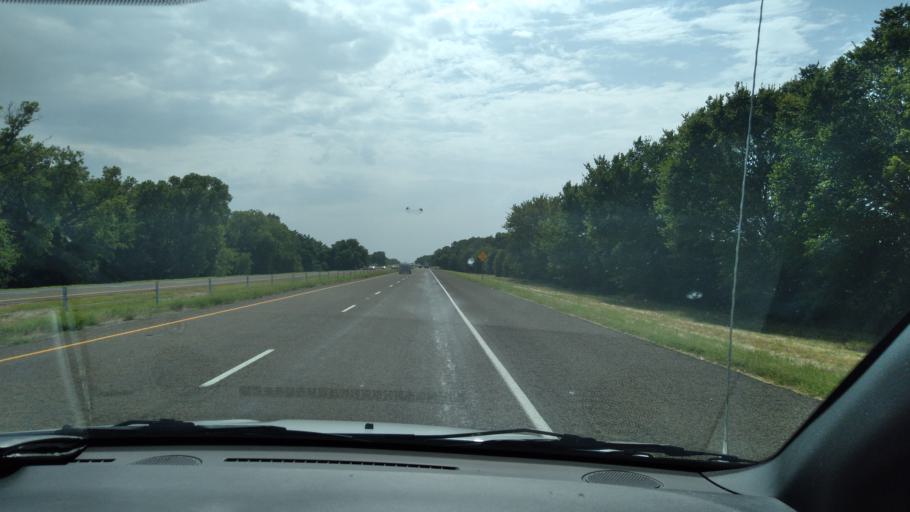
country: US
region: Texas
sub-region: Navarro County
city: Kerens
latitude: 32.1253
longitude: -96.2770
